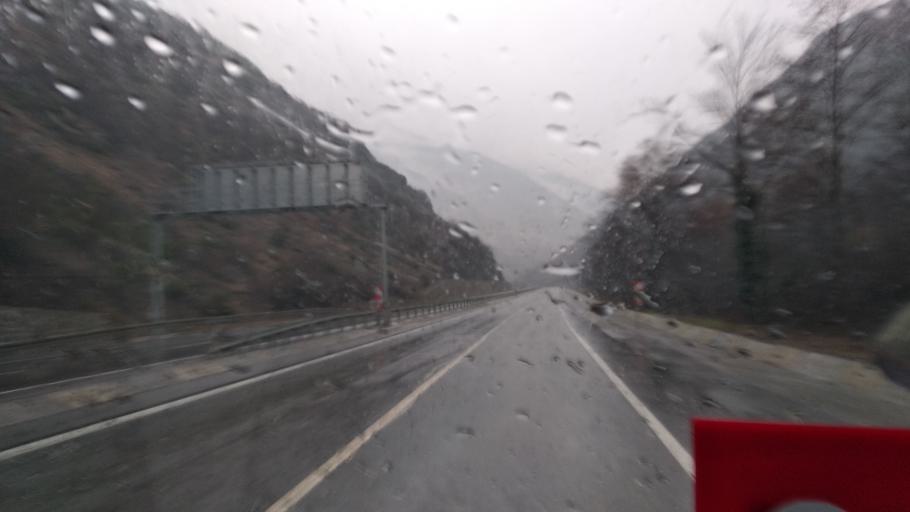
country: TR
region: Trabzon
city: Macka
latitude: 40.7920
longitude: 39.5814
